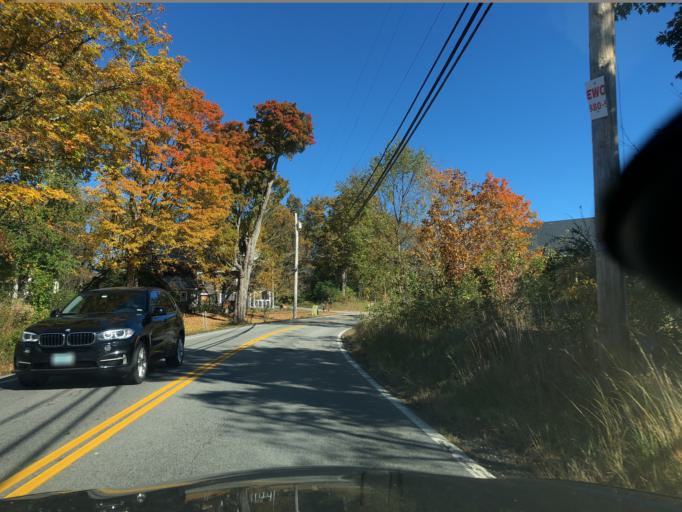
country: US
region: New Hampshire
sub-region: Rockingham County
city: Exeter
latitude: 43.0134
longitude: -70.9456
